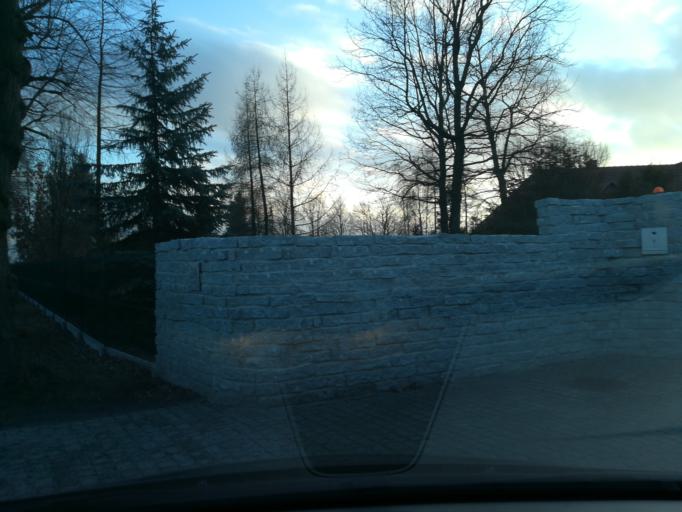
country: PL
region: Lodz Voivodeship
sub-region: Piotrkow Trybunalski
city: Piotrkow Trybunalski
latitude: 51.4104
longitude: 19.6475
